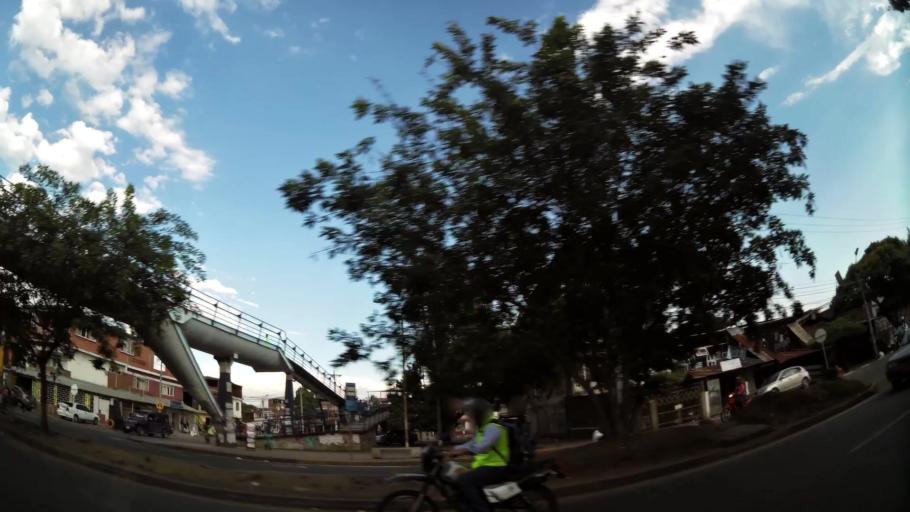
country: CO
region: Valle del Cauca
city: Cali
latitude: 3.4461
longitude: -76.4894
